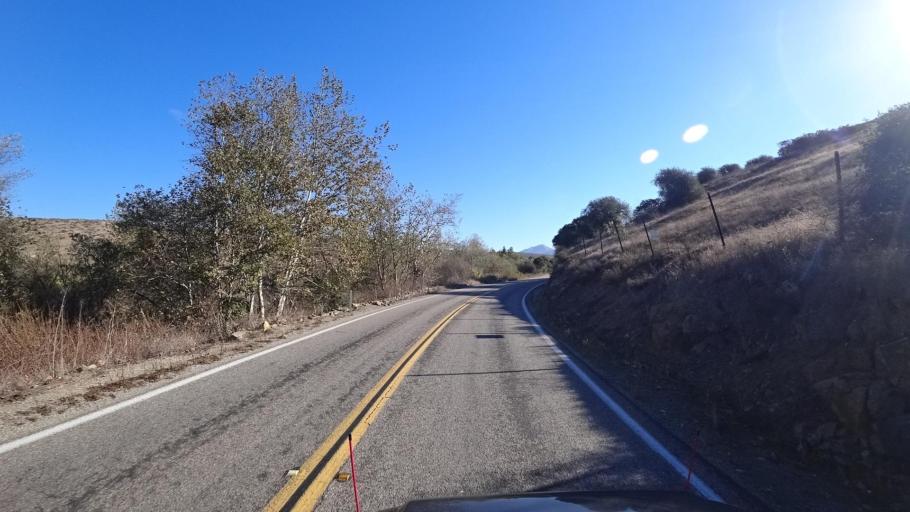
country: US
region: California
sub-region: San Diego County
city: Jamul
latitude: 32.6494
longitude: -116.8688
